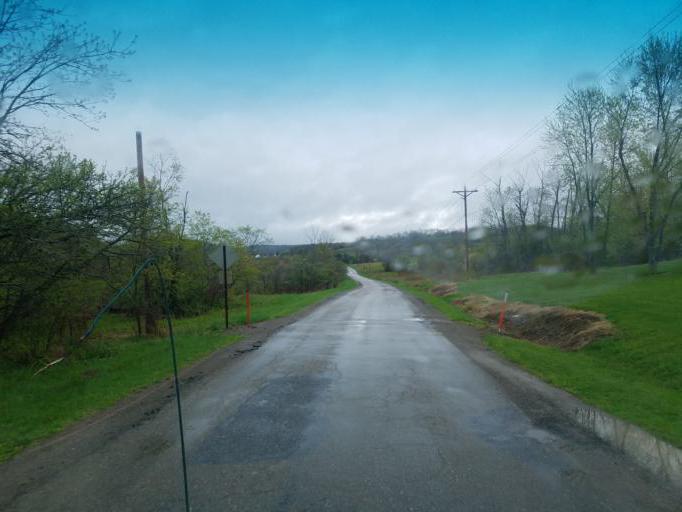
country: US
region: Pennsylvania
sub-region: Tioga County
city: Westfield
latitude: 41.9754
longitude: -77.6720
